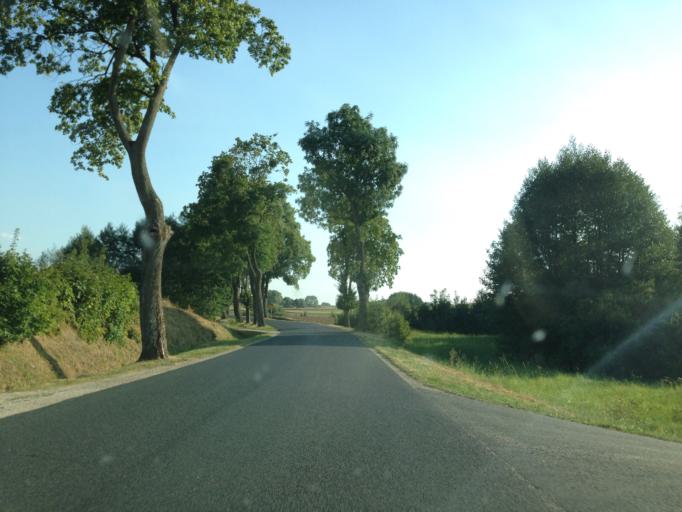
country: PL
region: Kujawsko-Pomorskie
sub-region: Powiat brodnicki
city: Brodnica
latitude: 53.3446
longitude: 19.3748
